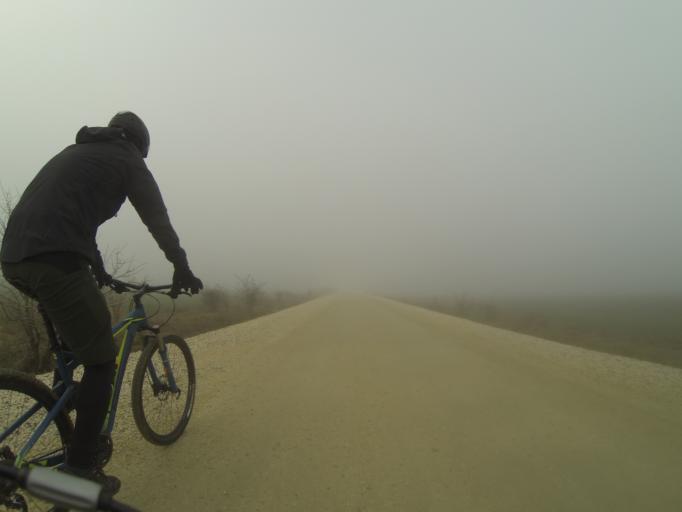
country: RO
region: Mehedinti
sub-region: Comuna Baclesu
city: Baclesu
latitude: 44.4404
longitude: 23.1343
